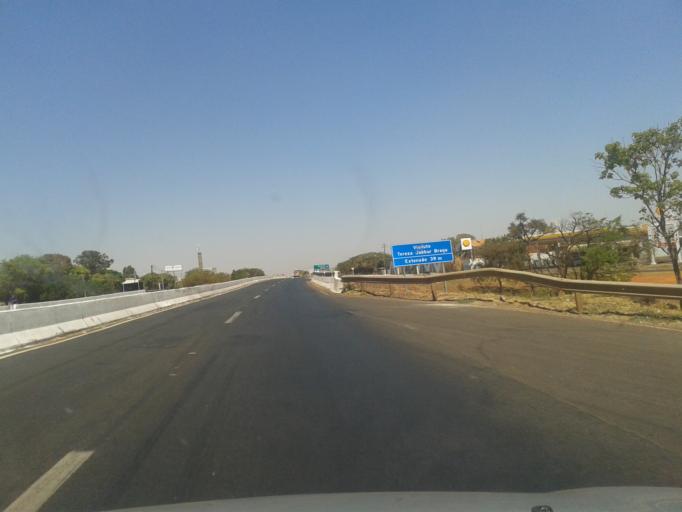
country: BR
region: Minas Gerais
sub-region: Uberlandia
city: Uberlandia
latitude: -18.9247
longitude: -48.2217
